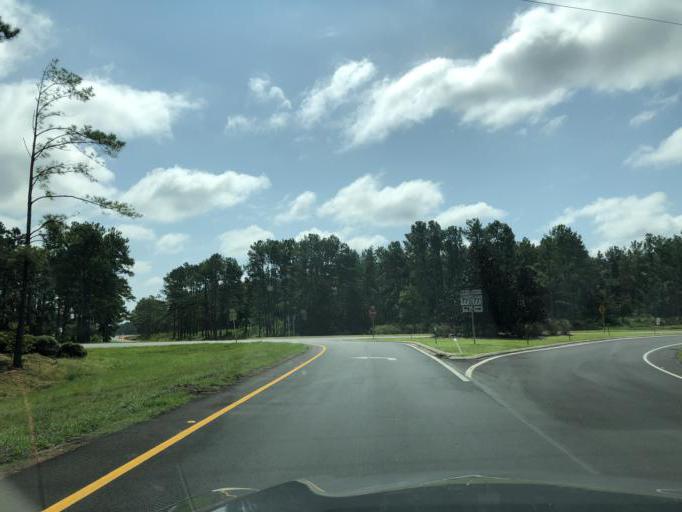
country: US
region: Florida
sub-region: Washington County
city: Chipley
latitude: 30.7474
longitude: -85.5528
